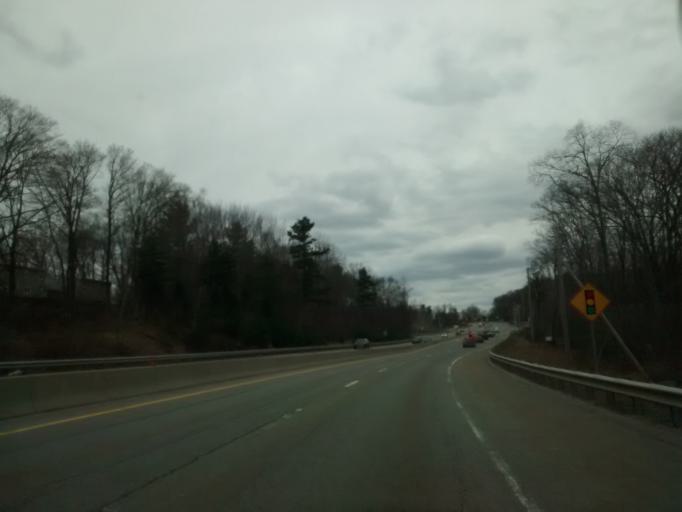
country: US
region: Massachusetts
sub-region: Worcester County
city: Charlton
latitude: 42.1471
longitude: -71.9369
